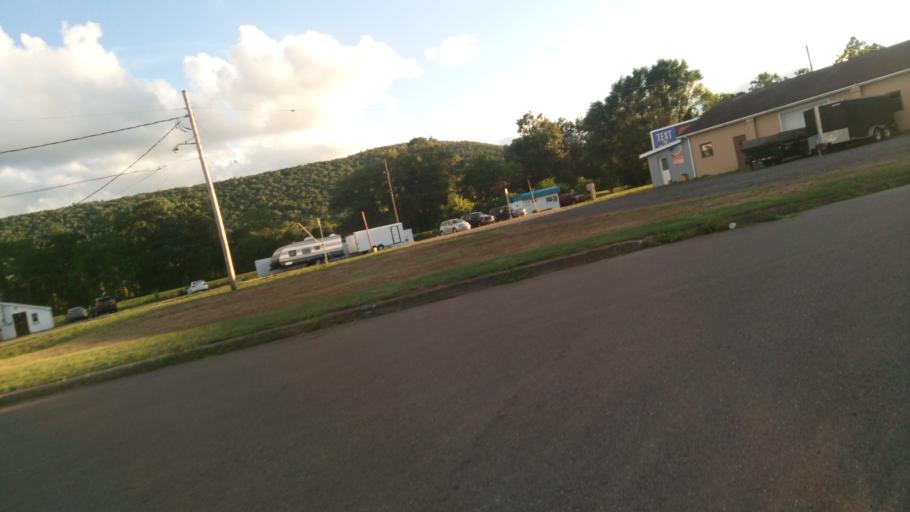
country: US
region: New York
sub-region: Chemung County
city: Southport
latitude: 42.0582
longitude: -76.7997
